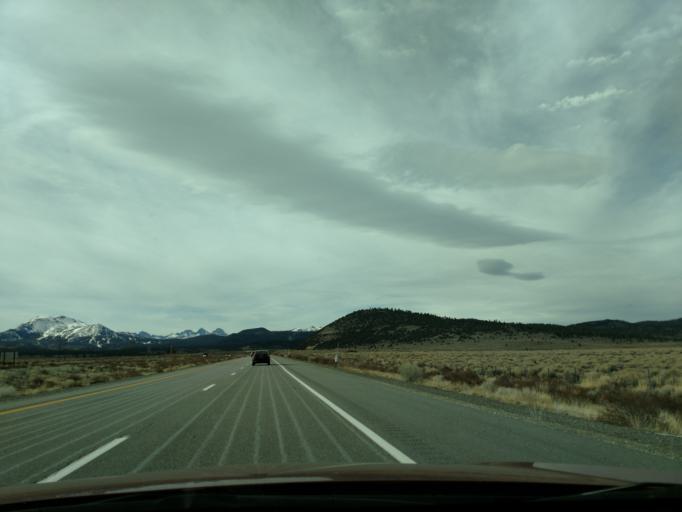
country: US
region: California
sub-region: Mono County
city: Mammoth Lakes
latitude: 37.6303
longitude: -118.8680
